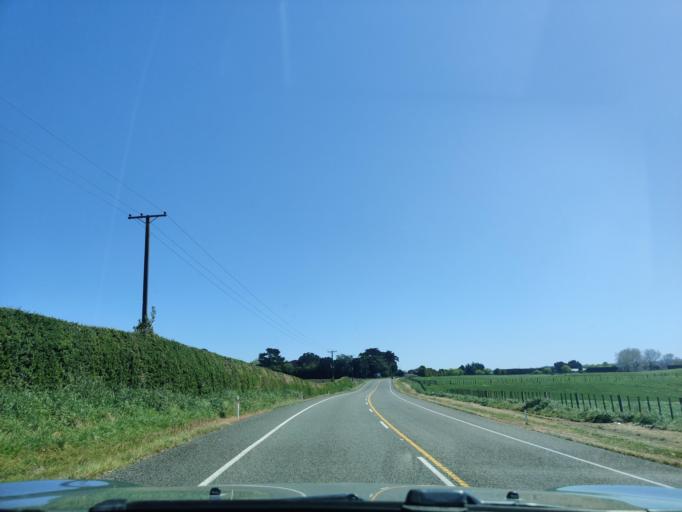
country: NZ
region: Taranaki
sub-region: South Taranaki District
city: Patea
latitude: -39.7951
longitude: 174.7069
